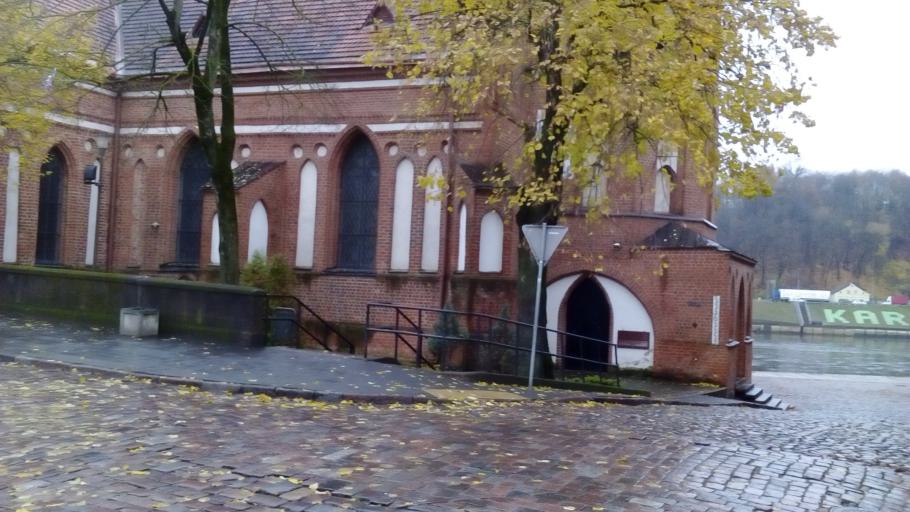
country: LT
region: Kauno apskritis
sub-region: Kaunas
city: Kaunas
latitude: 54.8954
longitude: 23.8865
